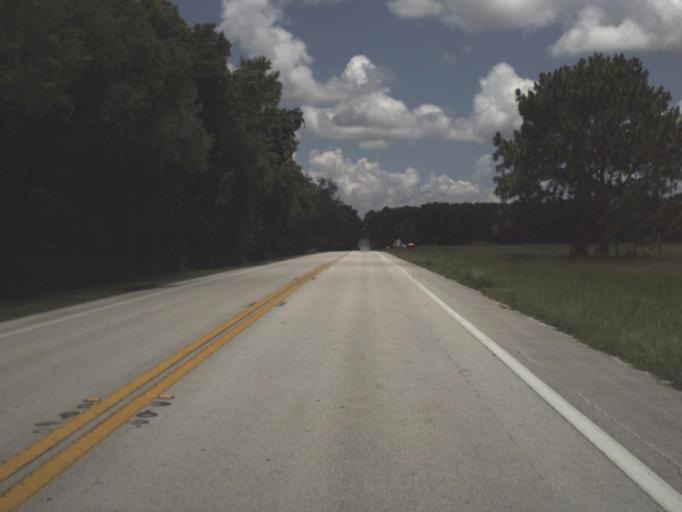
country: US
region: Florida
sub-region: Putnam County
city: Palatka
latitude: 29.5434
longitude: -81.6496
